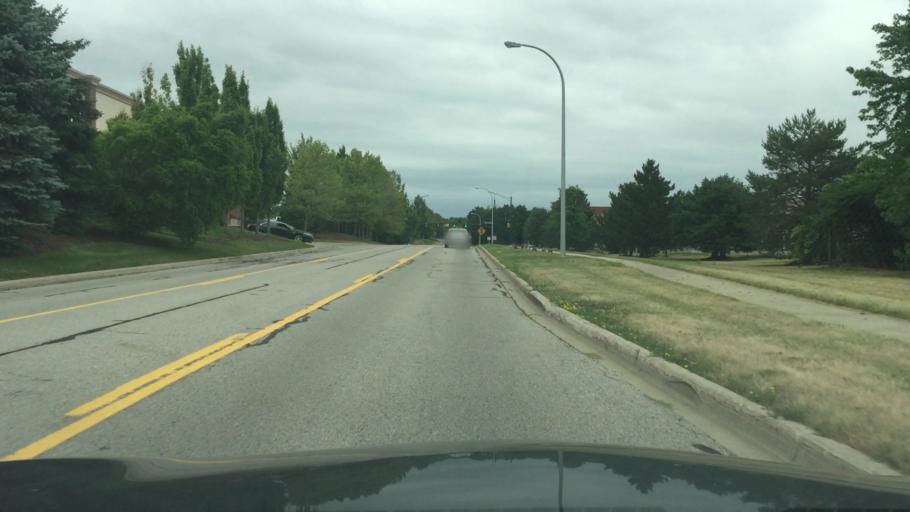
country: US
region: Michigan
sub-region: Oakland County
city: Novi
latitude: 42.4898
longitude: -83.4821
